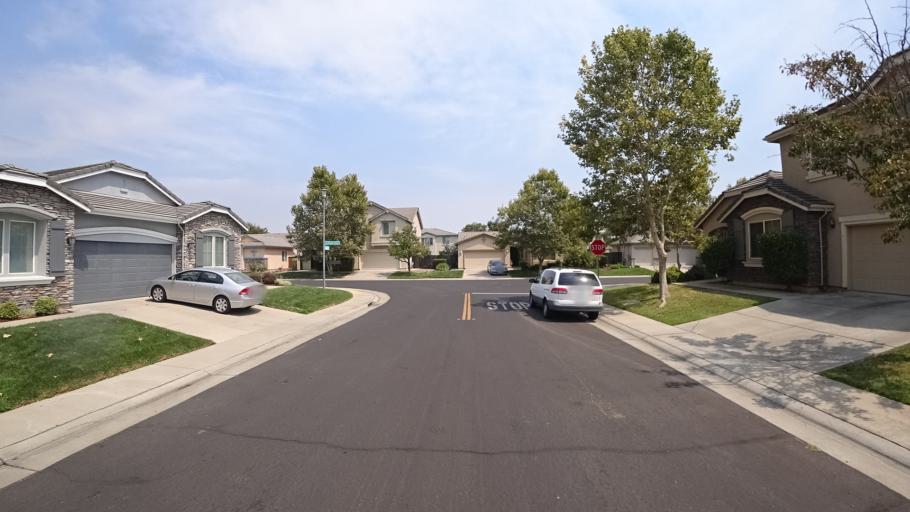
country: US
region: California
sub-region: Sacramento County
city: Laguna
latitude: 38.3835
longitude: -121.4276
